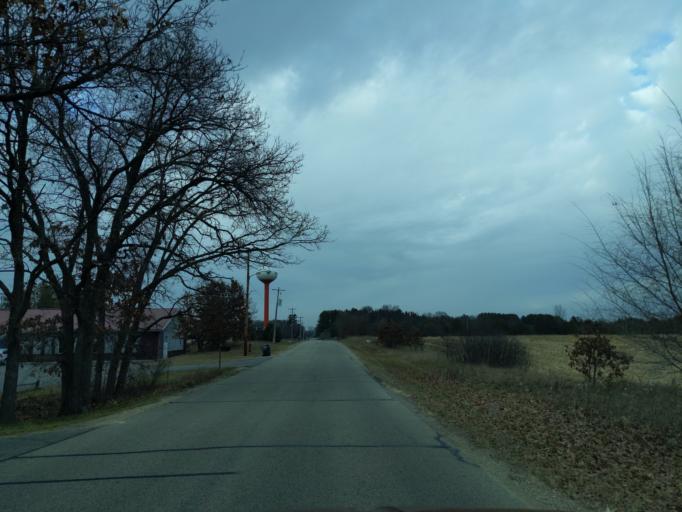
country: US
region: Wisconsin
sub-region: Waushara County
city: Wautoma
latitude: 44.0633
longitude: -89.2774
